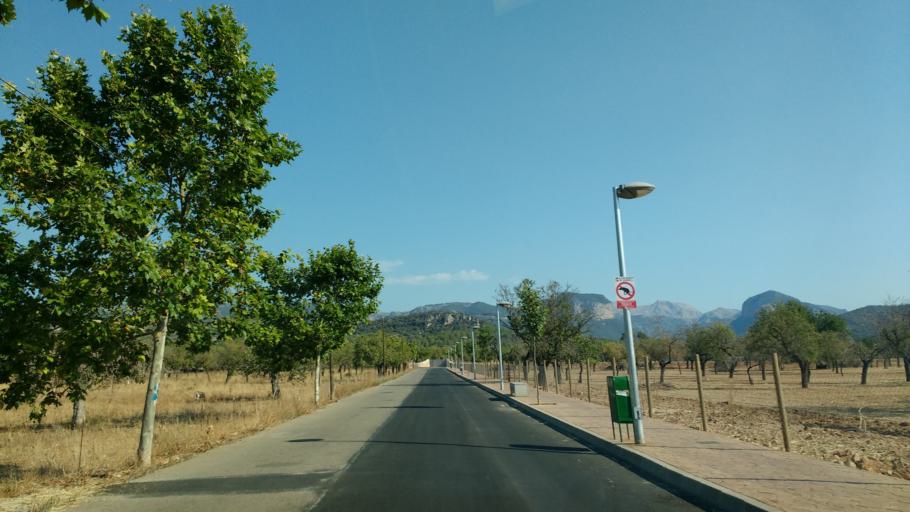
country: ES
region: Balearic Islands
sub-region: Illes Balears
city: Consell
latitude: 39.6724
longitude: 2.8105
